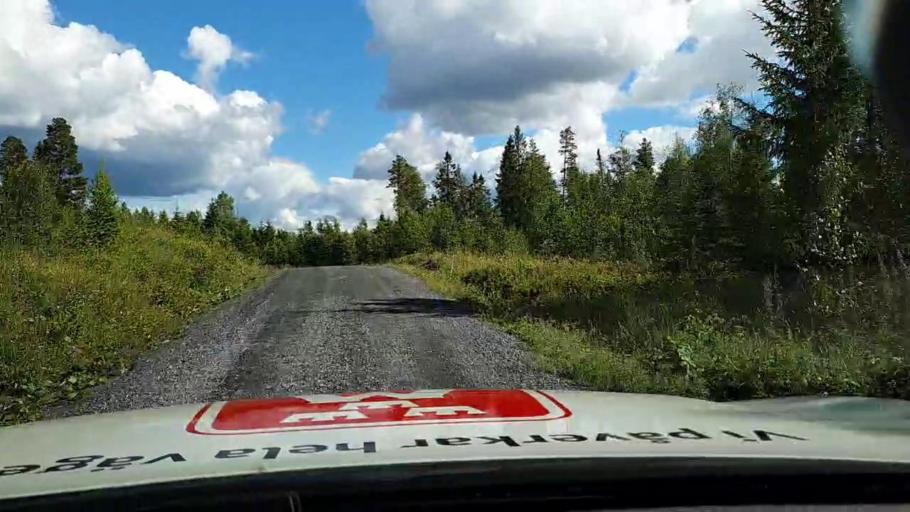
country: SE
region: Jaemtland
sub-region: Krokoms Kommun
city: Valla
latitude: 63.3270
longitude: 13.7368
